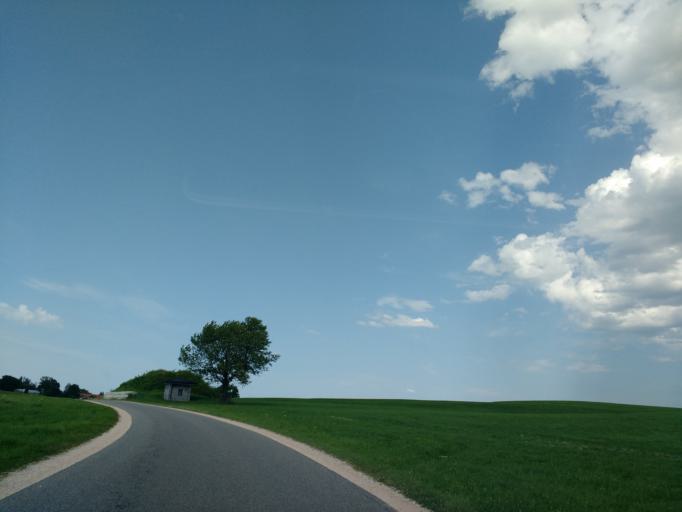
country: DE
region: Bavaria
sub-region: Upper Bavaria
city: Obing
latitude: 48.0088
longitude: 12.4398
